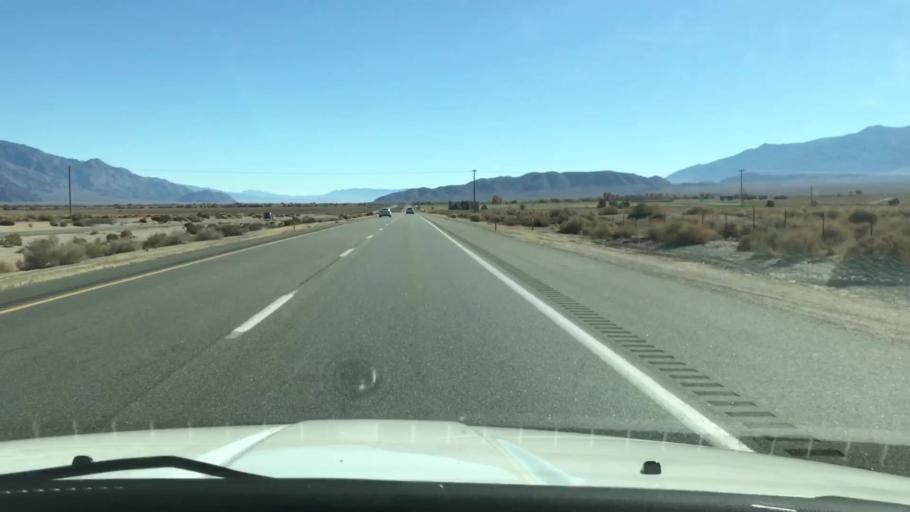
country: US
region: California
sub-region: Inyo County
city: Lone Pine
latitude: 36.7622
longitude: -118.1706
